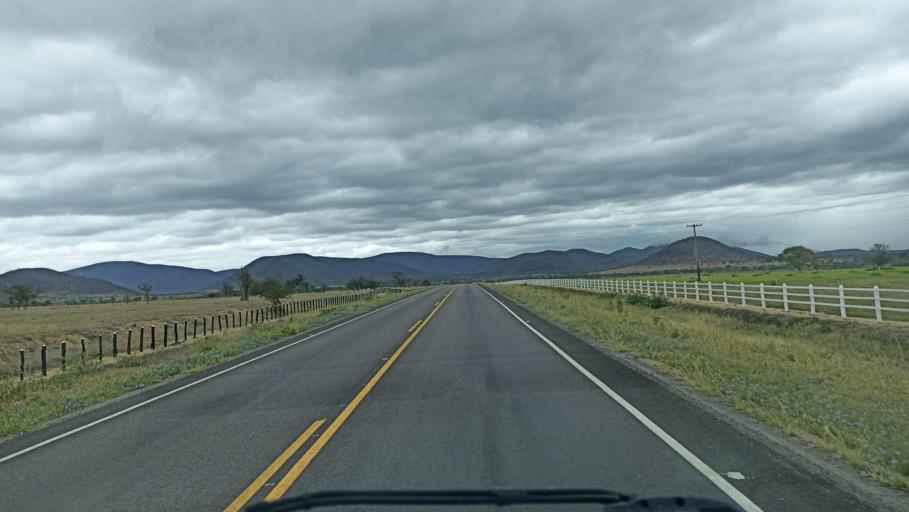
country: BR
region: Bahia
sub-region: Iacu
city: Iacu
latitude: -12.9159
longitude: -40.4116
